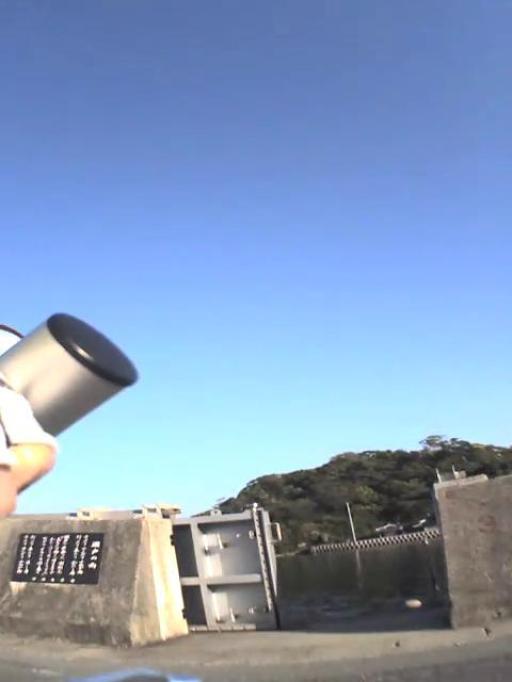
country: JP
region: Yamaguchi
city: Nagato
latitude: 34.3975
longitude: 131.1981
